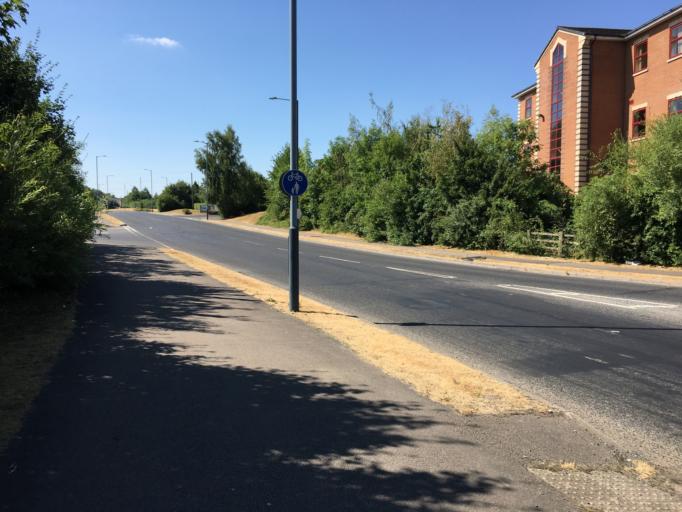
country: GB
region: England
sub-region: Warwickshire
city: Rugby
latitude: 52.4042
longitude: -1.2433
